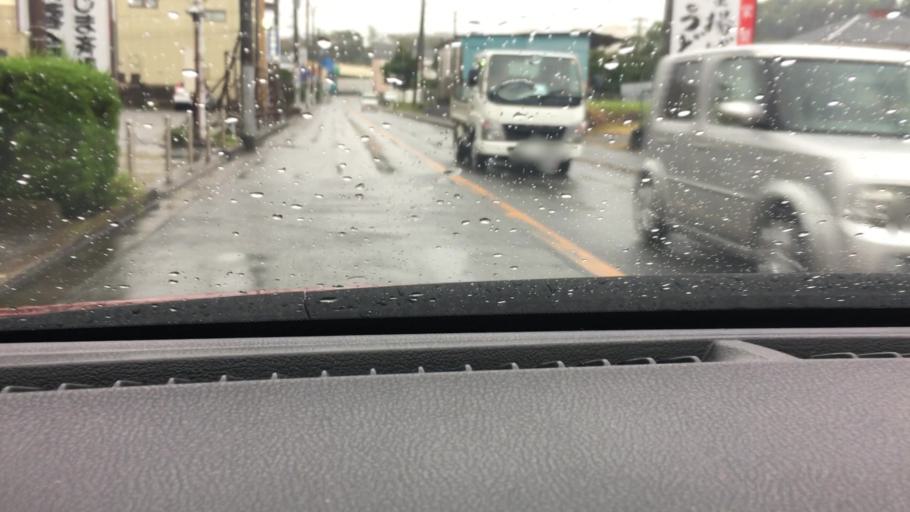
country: JP
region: Chiba
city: Kisarazu
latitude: 35.3750
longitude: 139.9349
